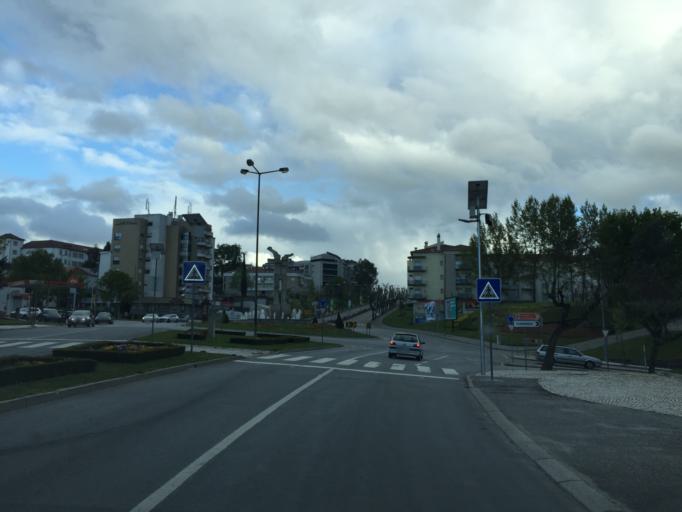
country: PT
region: Viseu
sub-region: Viseu
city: Viseu
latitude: 40.6603
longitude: -7.9238
